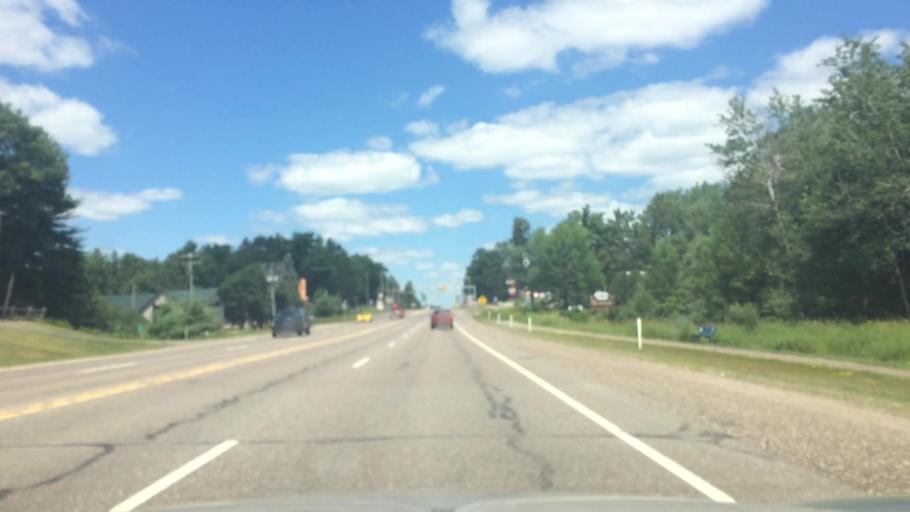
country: US
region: Wisconsin
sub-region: Vilas County
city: Lac du Flambeau
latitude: 45.9182
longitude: -89.6951
